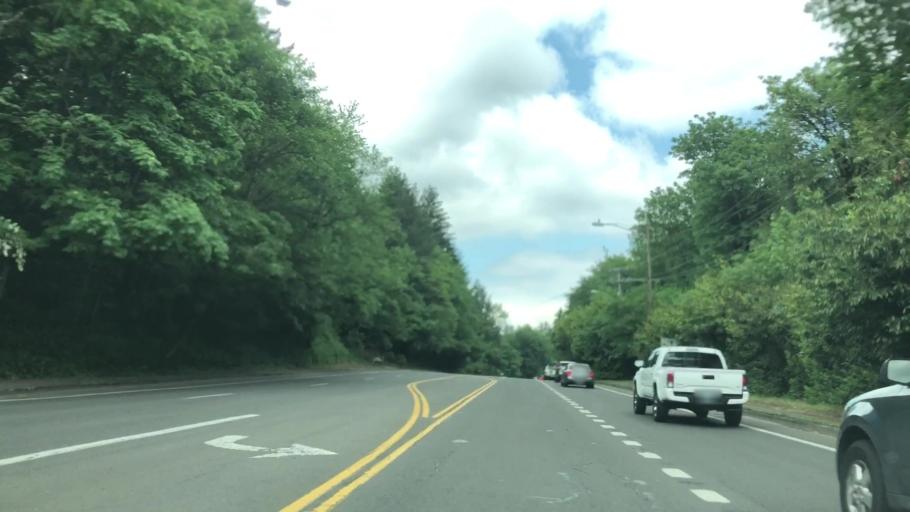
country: US
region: Oregon
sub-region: Clackamas County
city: Lake Oswego
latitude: 45.4224
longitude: -122.7097
